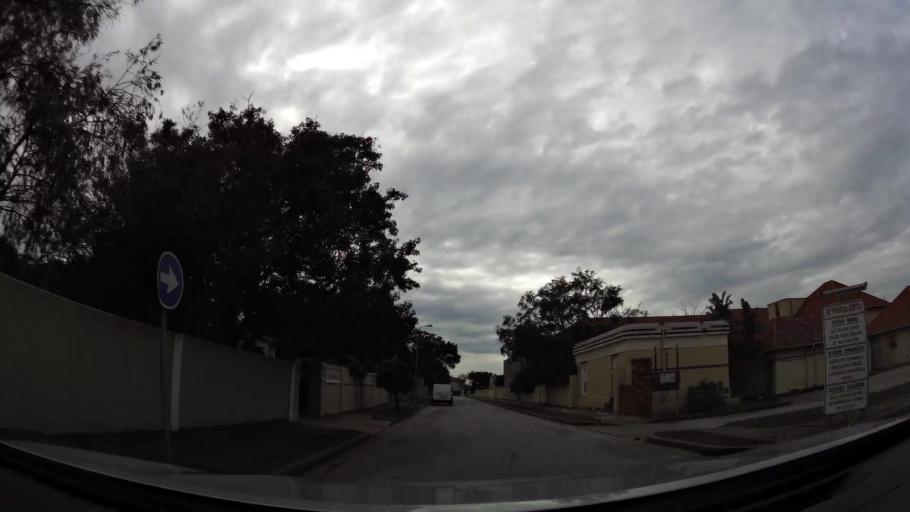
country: ZA
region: Eastern Cape
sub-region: Nelson Mandela Bay Metropolitan Municipality
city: Port Elizabeth
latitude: -33.9571
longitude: 25.5977
